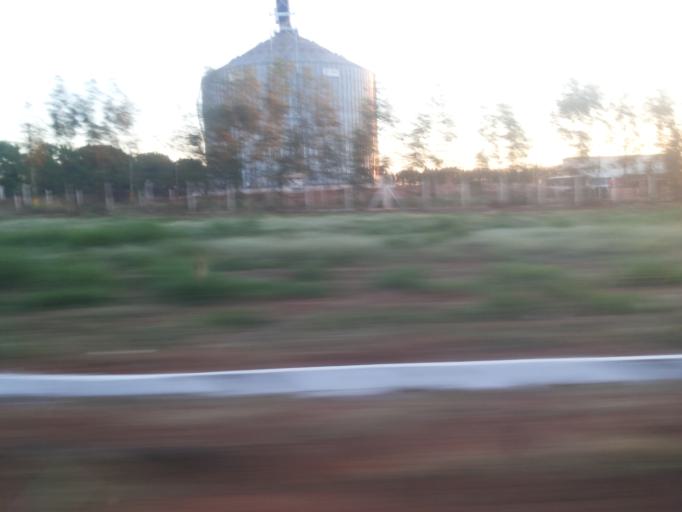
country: BR
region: Minas Gerais
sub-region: Capinopolis
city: Capinopolis
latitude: -18.7406
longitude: -49.5490
